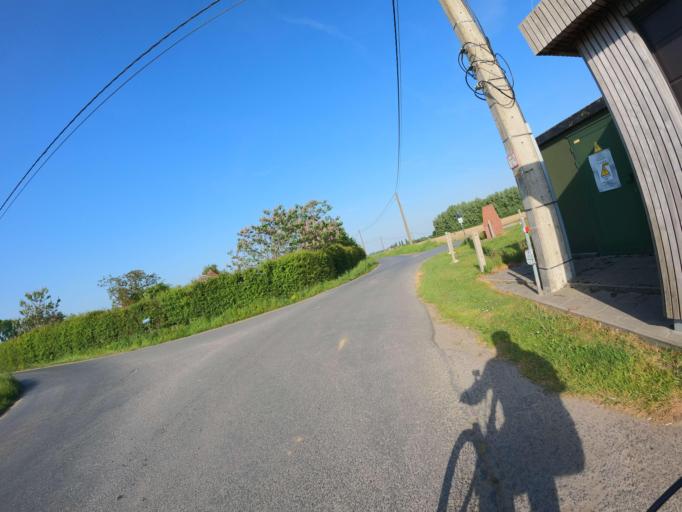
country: BE
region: Flanders
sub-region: Provincie West-Vlaanderen
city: Tielt
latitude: 51.0144
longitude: 3.3468
